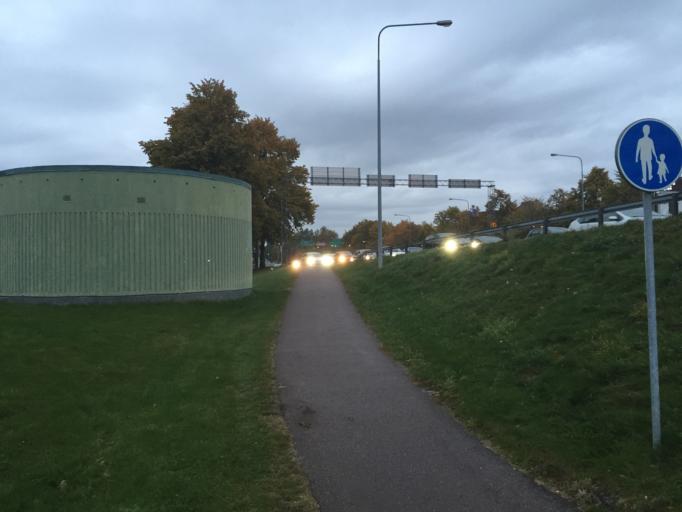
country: SE
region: Vaermland
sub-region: Karlstads Kommun
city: Karlstad
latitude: 59.3817
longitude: 13.4882
